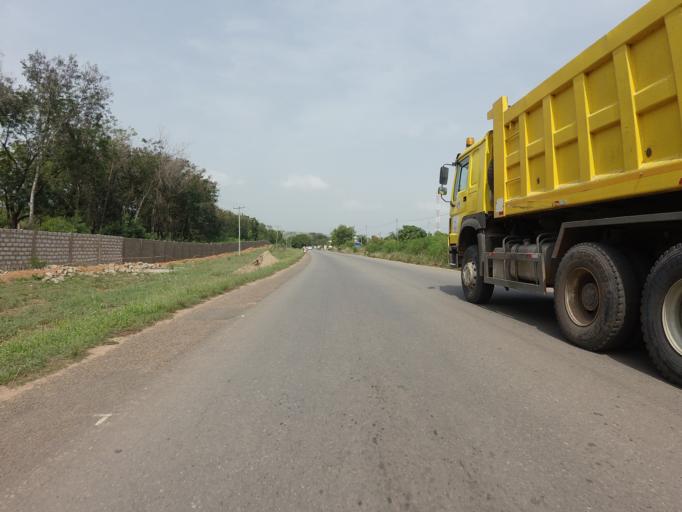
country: GH
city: Akropong
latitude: 6.2516
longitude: 0.0837
